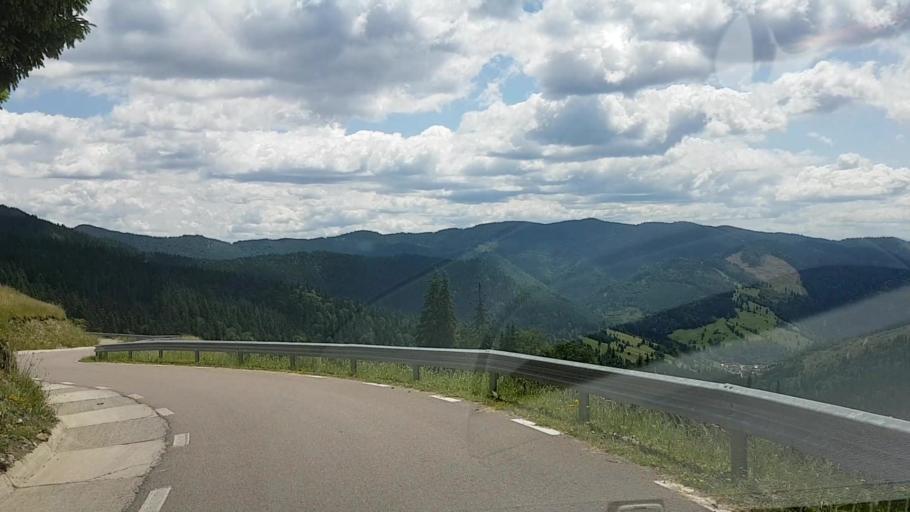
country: RO
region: Suceava
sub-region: Municipiul Campulung Moldovenesc
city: Campulung Moldovenesc
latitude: 47.4370
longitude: 25.5596
